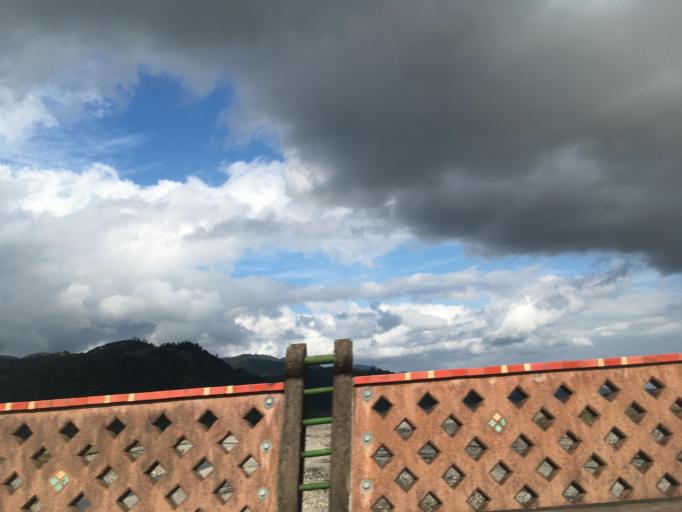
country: TW
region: Taiwan
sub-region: Yilan
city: Yilan
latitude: 24.6691
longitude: 121.6103
